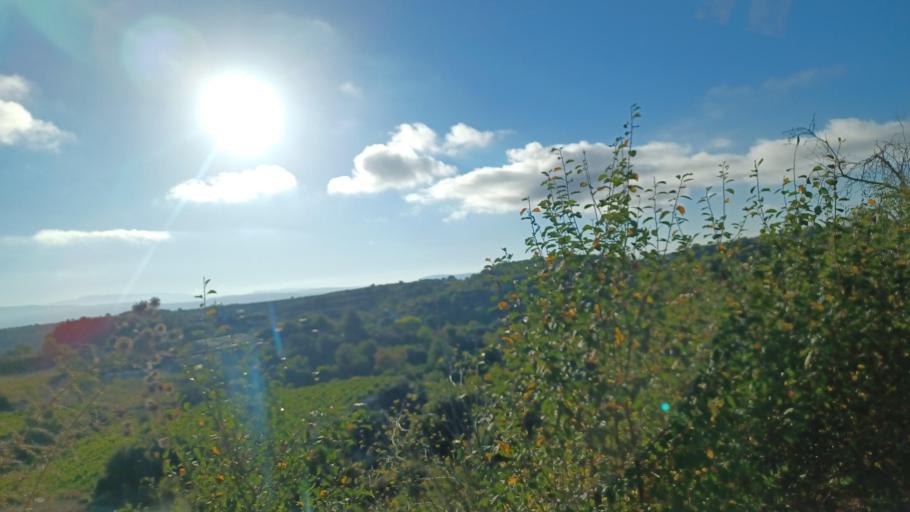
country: CY
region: Pafos
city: Tala
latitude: 34.8526
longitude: 32.4576
